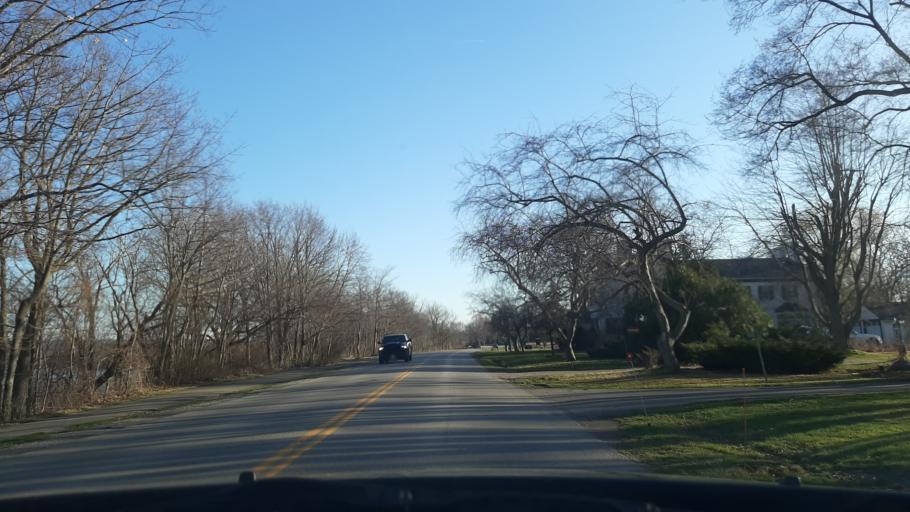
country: US
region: New York
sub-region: Niagara County
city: Youngstown
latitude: 43.2145
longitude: -79.0607
